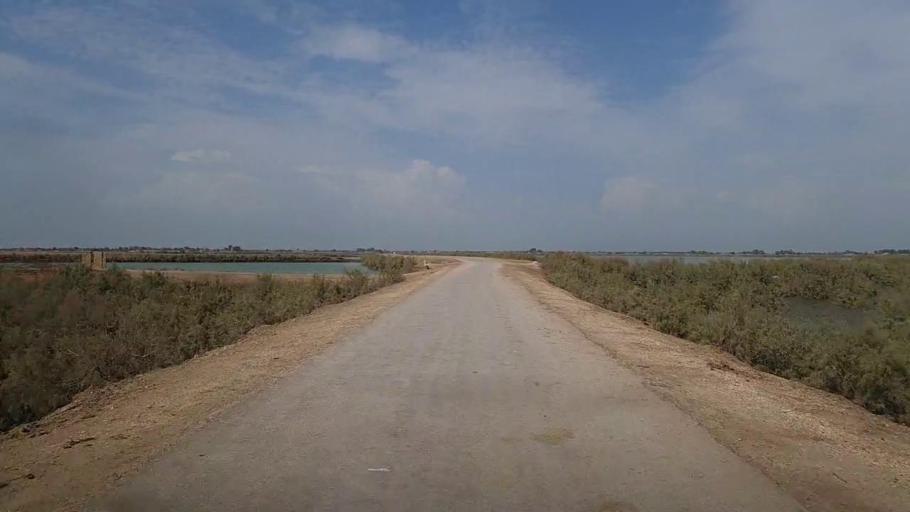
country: PK
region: Sindh
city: Thul
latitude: 28.2772
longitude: 68.8213
